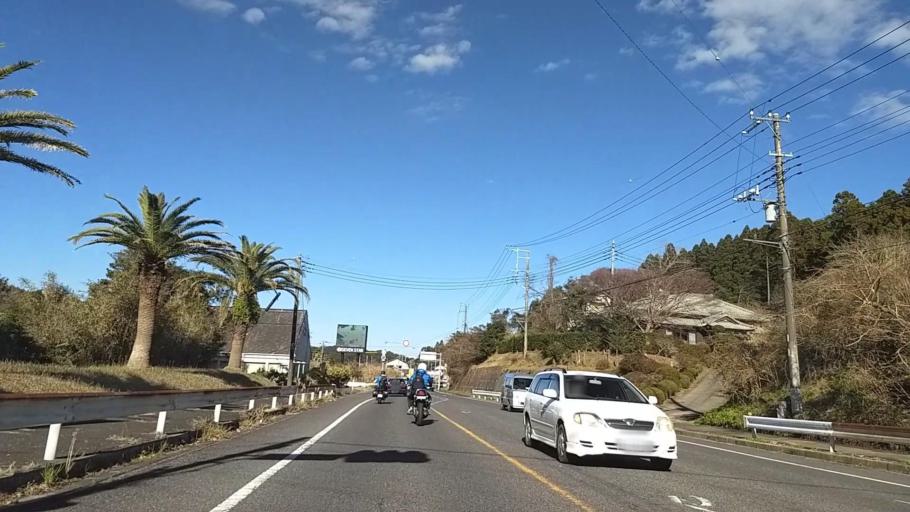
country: JP
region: Chiba
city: Ohara
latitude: 35.2110
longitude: 140.3756
